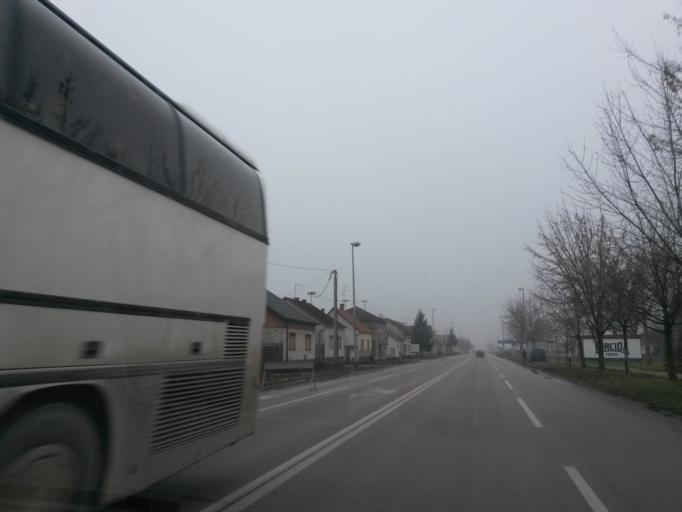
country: HR
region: Vukovarsko-Srijemska
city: Zupanja
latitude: 45.0807
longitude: 18.6955
